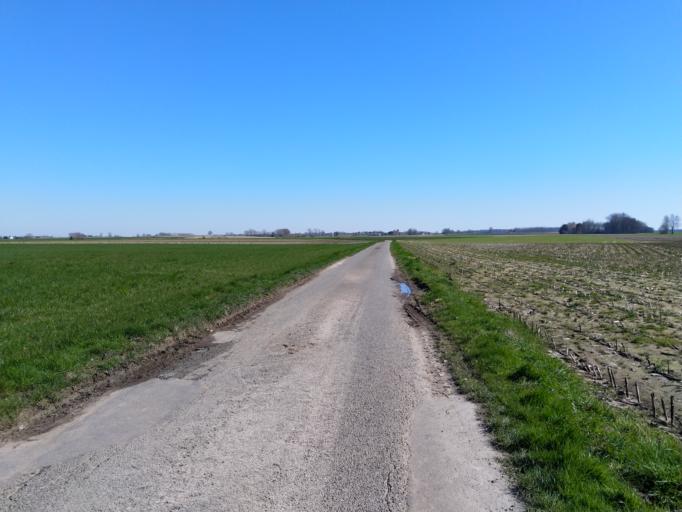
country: BE
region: Wallonia
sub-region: Province du Hainaut
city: Jurbise
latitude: 50.5518
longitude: 3.9311
